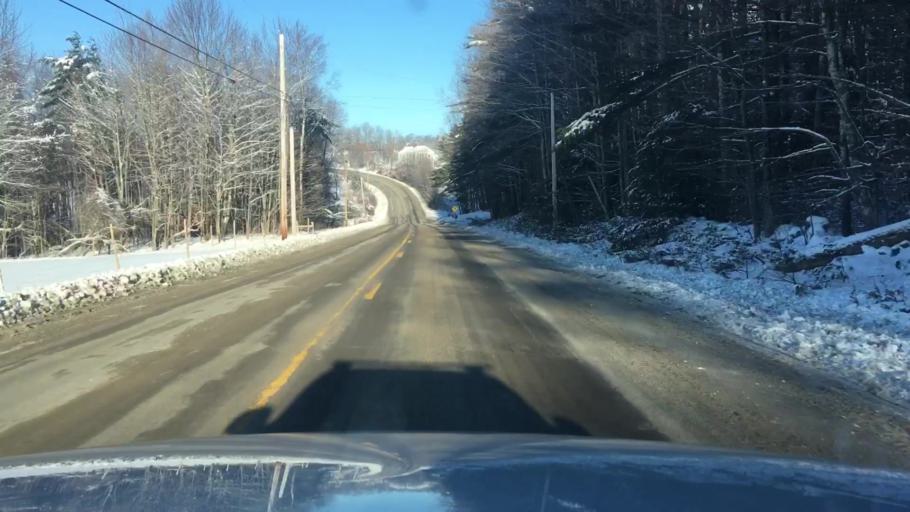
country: US
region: Maine
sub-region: Kennebec County
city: Readfield
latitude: 44.4276
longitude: -69.9354
